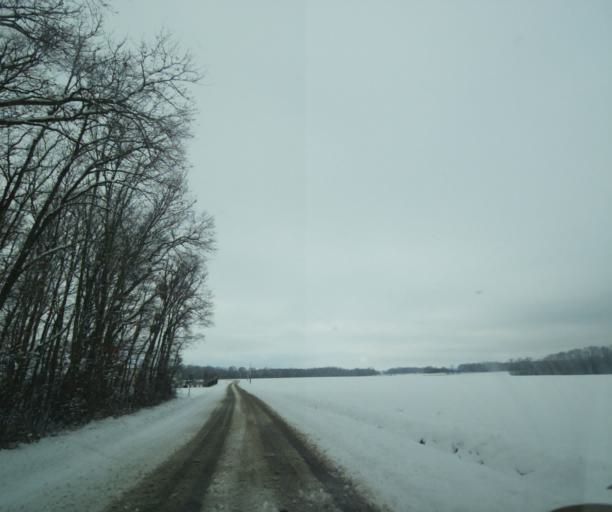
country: FR
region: Champagne-Ardenne
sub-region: Departement de la Haute-Marne
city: Montier-en-Der
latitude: 48.5305
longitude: 4.7480
